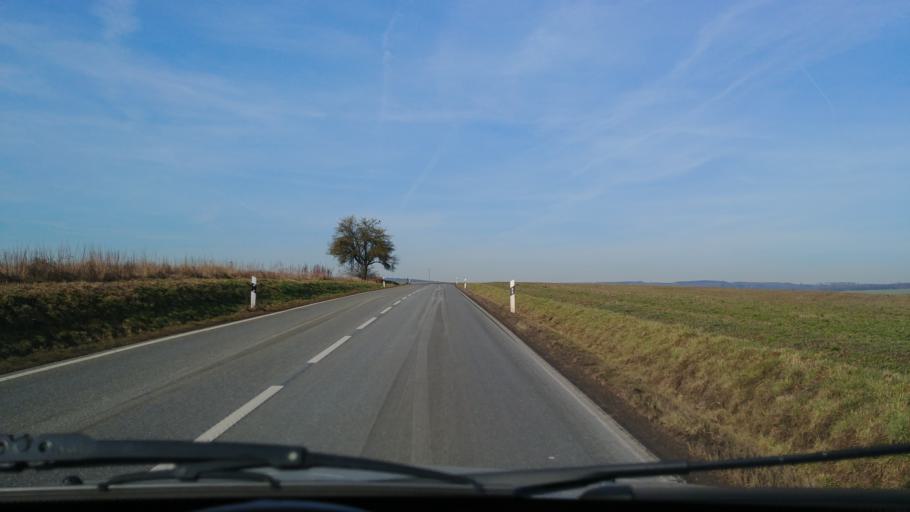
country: DE
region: Rheinland-Pfalz
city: Geisig
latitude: 50.2434
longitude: 7.7971
